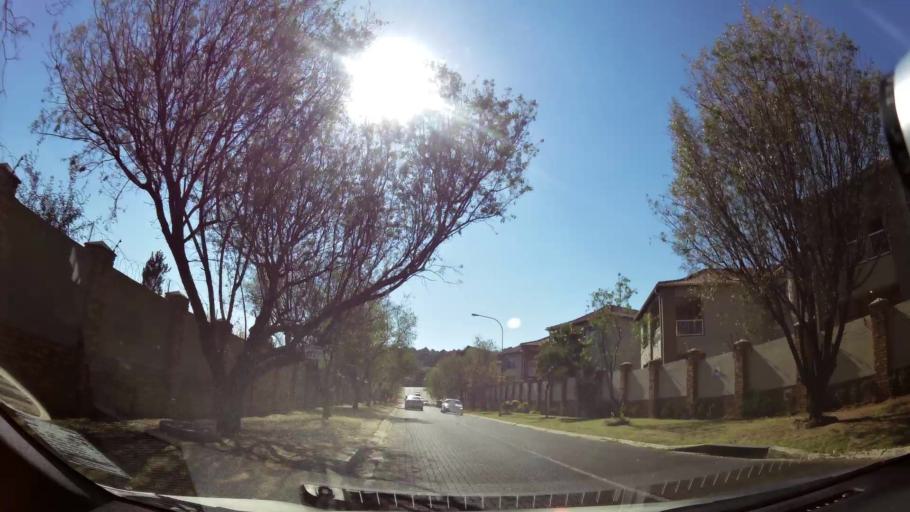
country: ZA
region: Gauteng
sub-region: City of Johannesburg Metropolitan Municipality
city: Johannesburg
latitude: -26.2673
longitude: 28.0145
